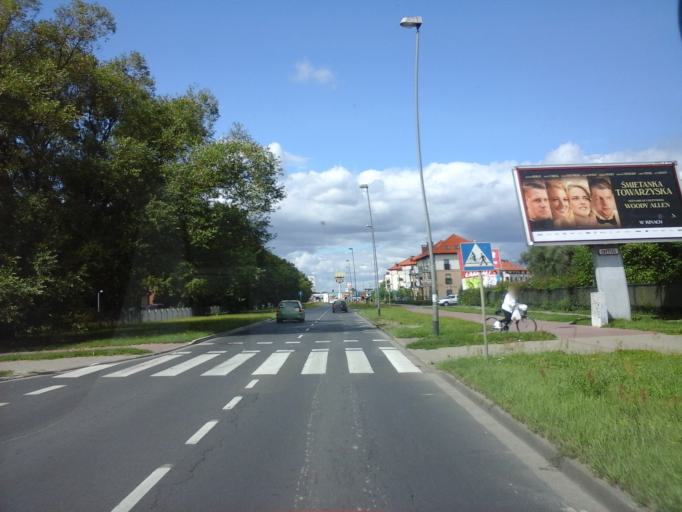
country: PL
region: West Pomeranian Voivodeship
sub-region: Powiat policki
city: Przeclaw
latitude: 53.4242
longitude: 14.4913
